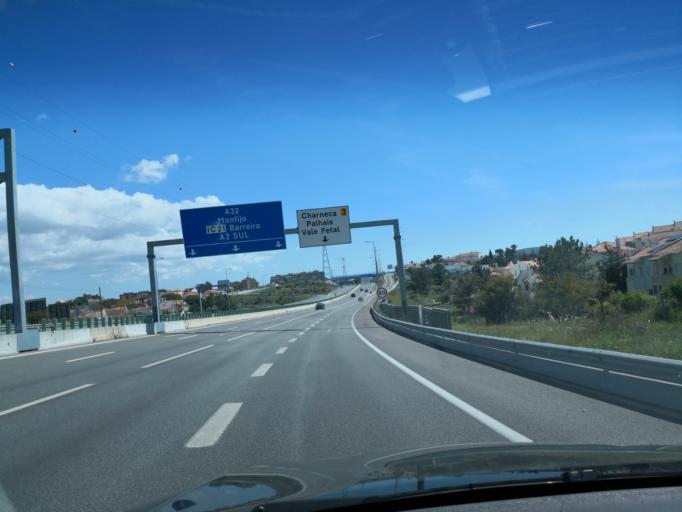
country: PT
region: Setubal
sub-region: Almada
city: Sobreda
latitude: 38.6359
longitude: -9.1966
